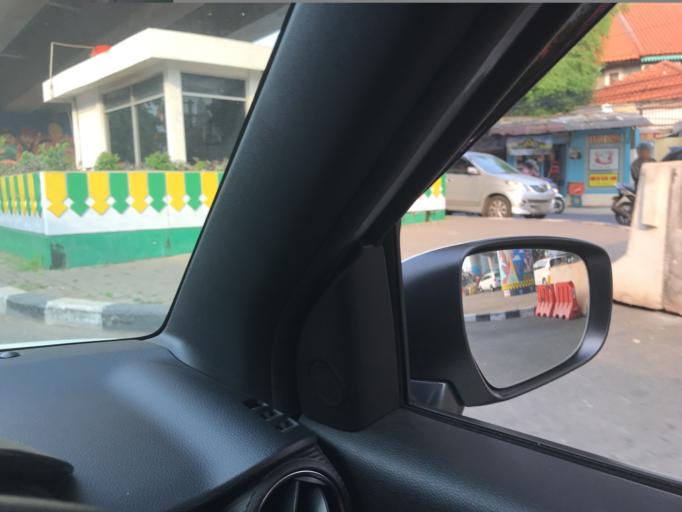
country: ID
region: Jakarta Raya
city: Jakarta
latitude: -6.2784
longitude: 106.8081
